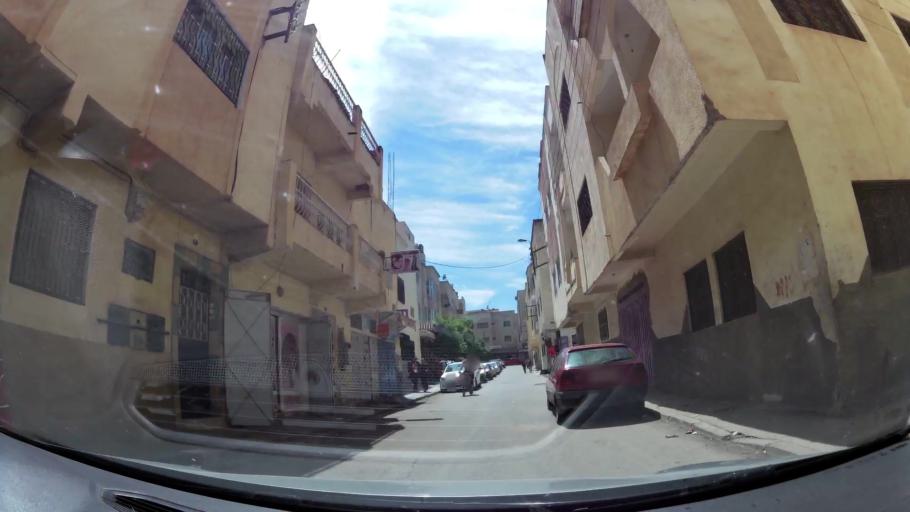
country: MA
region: Fes-Boulemane
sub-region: Fes
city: Fes
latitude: 34.0087
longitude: -4.9867
